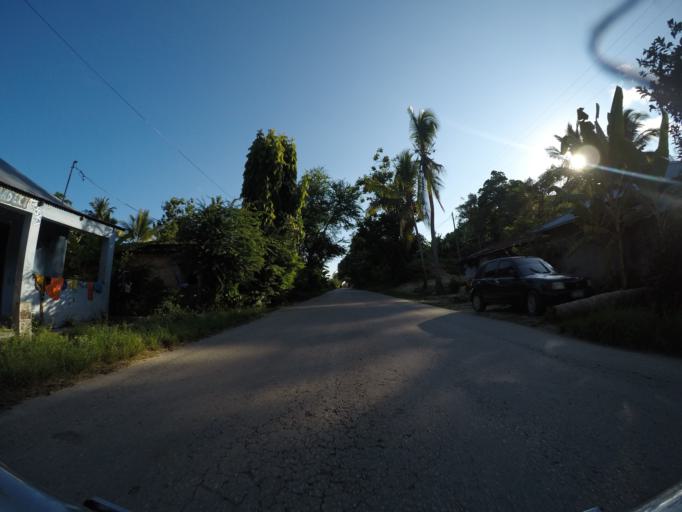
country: TZ
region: Pemba South
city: Chake Chake
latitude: -5.3181
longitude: 39.7432
